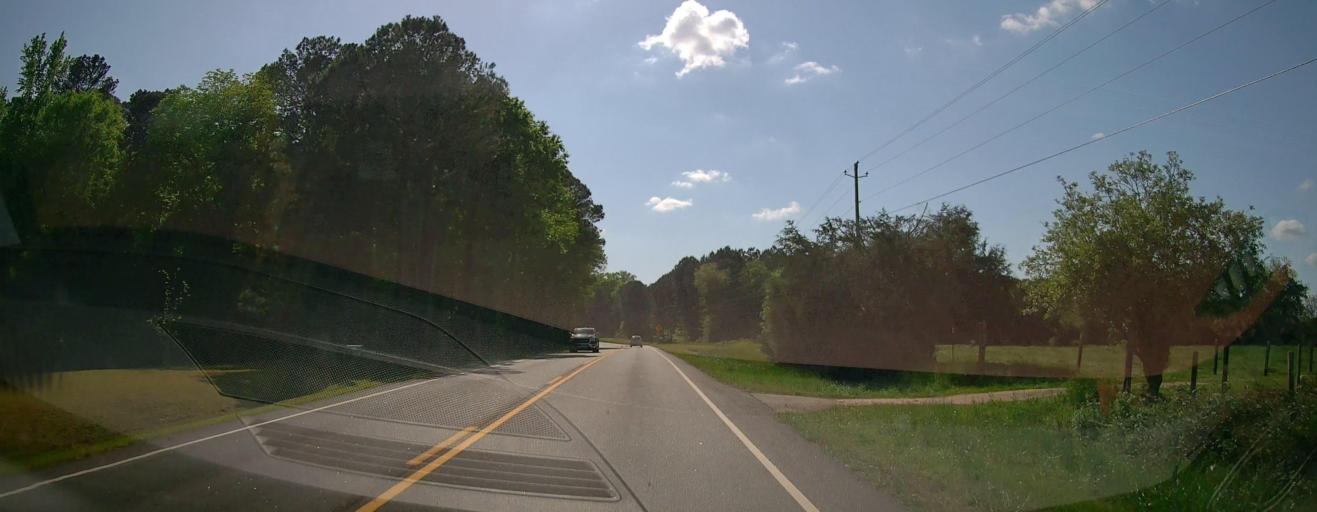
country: US
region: Georgia
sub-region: Morgan County
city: Madison
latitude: 33.6069
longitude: -83.3865
